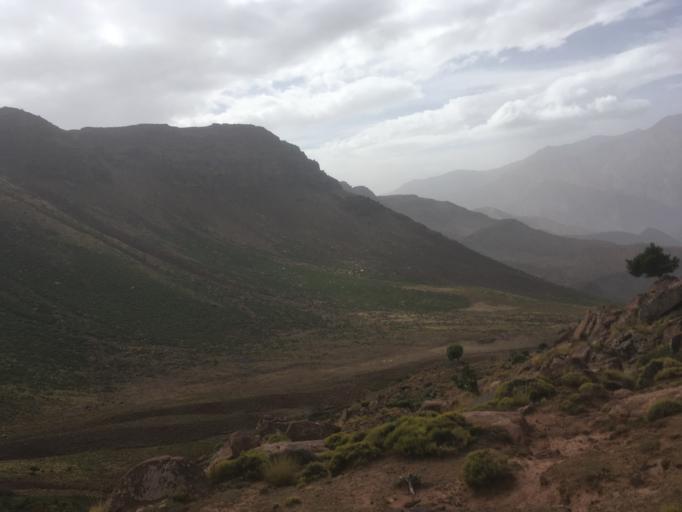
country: MA
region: Marrakech-Tensift-Al Haouz
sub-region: Al-Haouz
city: Tidili Mesfioua
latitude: 31.3234
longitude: -7.6701
